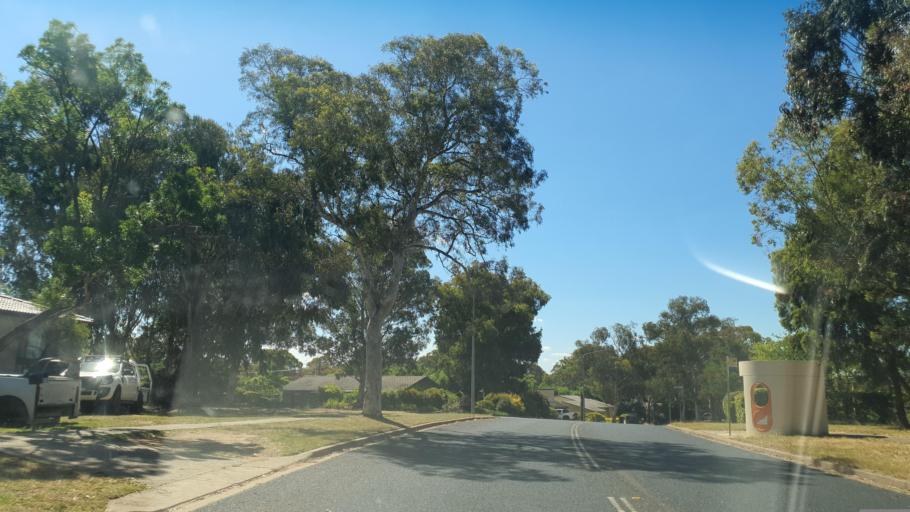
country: AU
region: Australian Capital Territory
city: Belconnen
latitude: -35.2122
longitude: 149.0437
